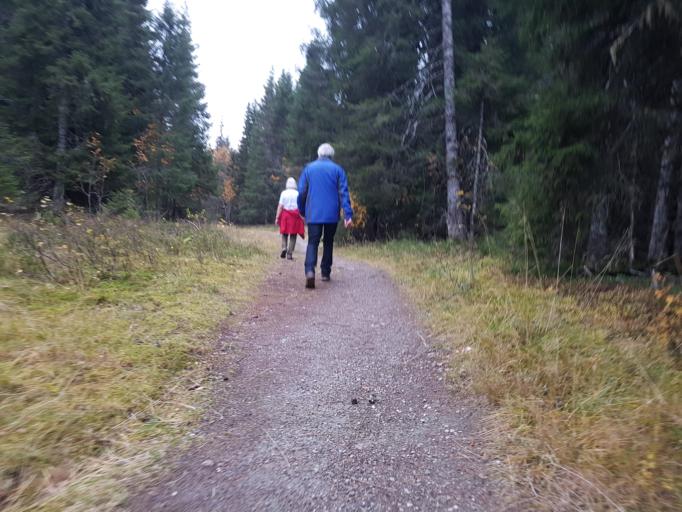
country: NO
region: Sor-Trondelag
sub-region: Melhus
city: Melhus
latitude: 63.3794
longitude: 10.2577
